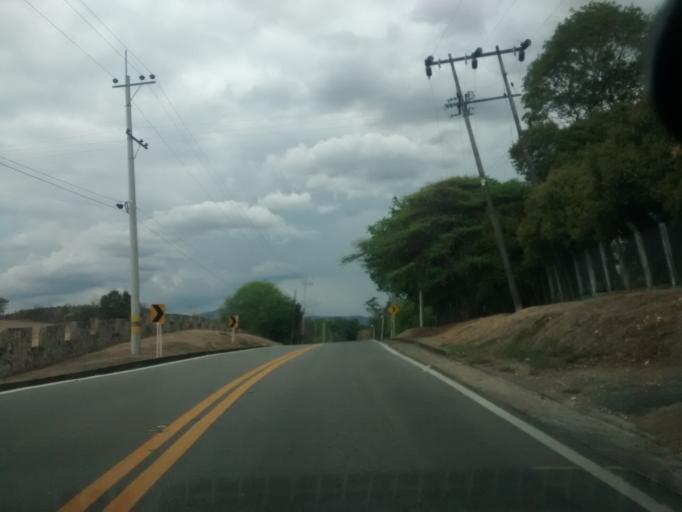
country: CO
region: Cundinamarca
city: Agua de Dios
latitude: 4.4246
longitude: -74.7014
